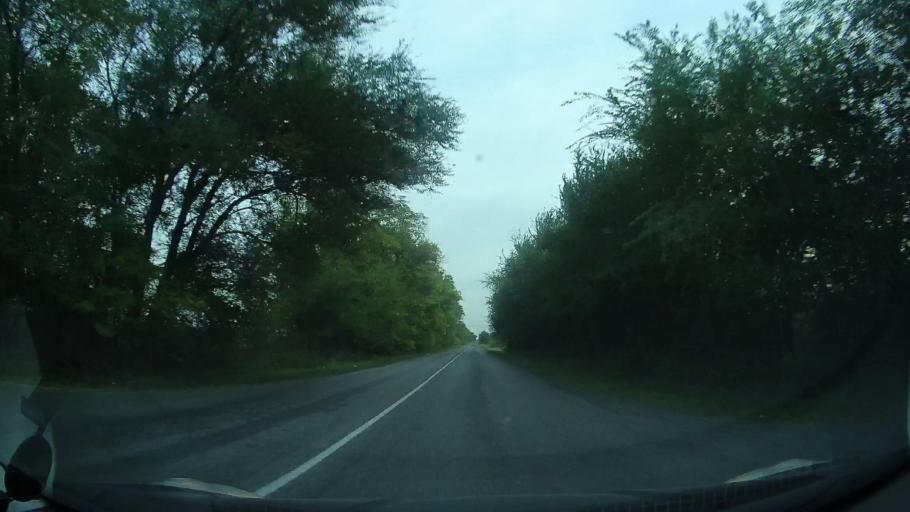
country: RU
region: Rostov
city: Ol'ginskaya
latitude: 47.1130
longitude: 39.9771
